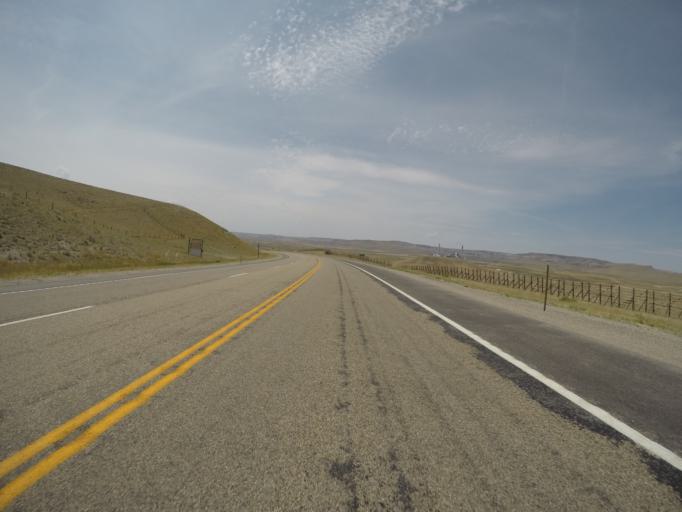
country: US
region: Wyoming
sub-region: Lincoln County
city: Kemmerer
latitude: 41.7687
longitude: -110.5567
